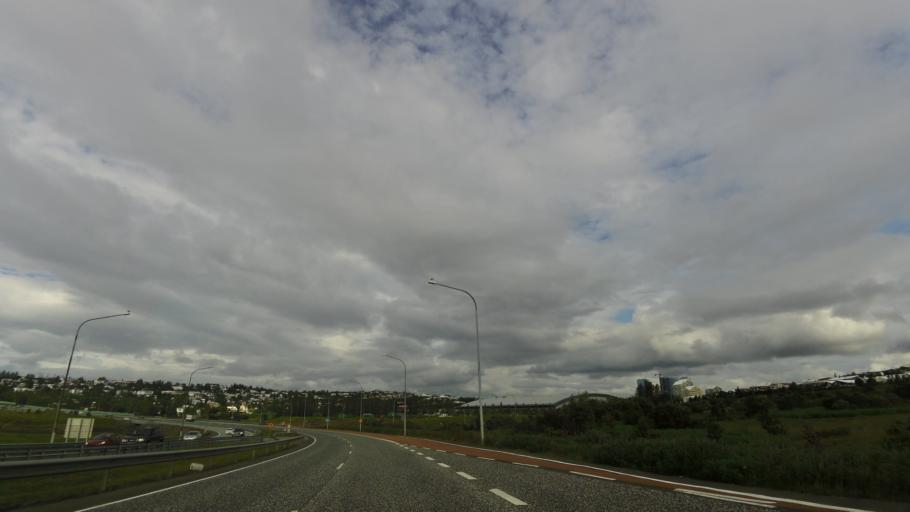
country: IS
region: Capital Region
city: Kopavogur
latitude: 64.1010
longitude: -21.9094
